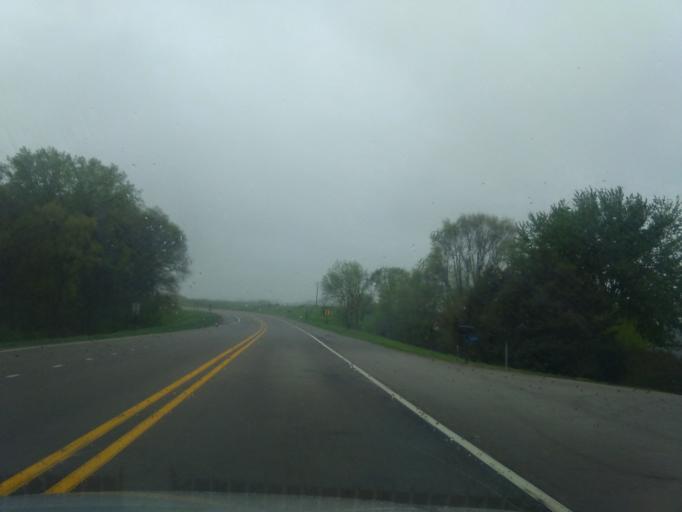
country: US
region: Nebraska
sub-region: Madison County
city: Norfolk
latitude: 42.1053
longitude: -97.3074
